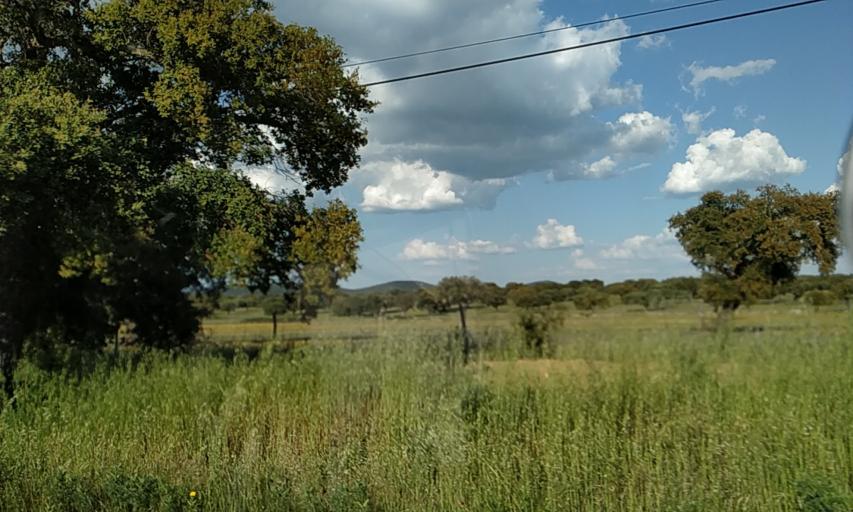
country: PT
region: Portalegre
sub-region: Portalegre
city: Urra
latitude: 39.1841
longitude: -7.4554
